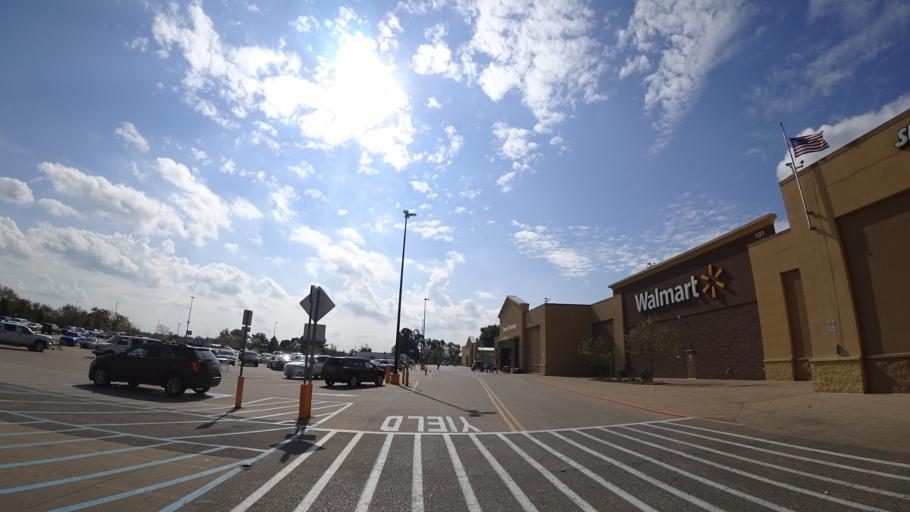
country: US
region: Michigan
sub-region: Saint Joseph County
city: Three Rivers
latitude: 41.9421
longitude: -85.6558
